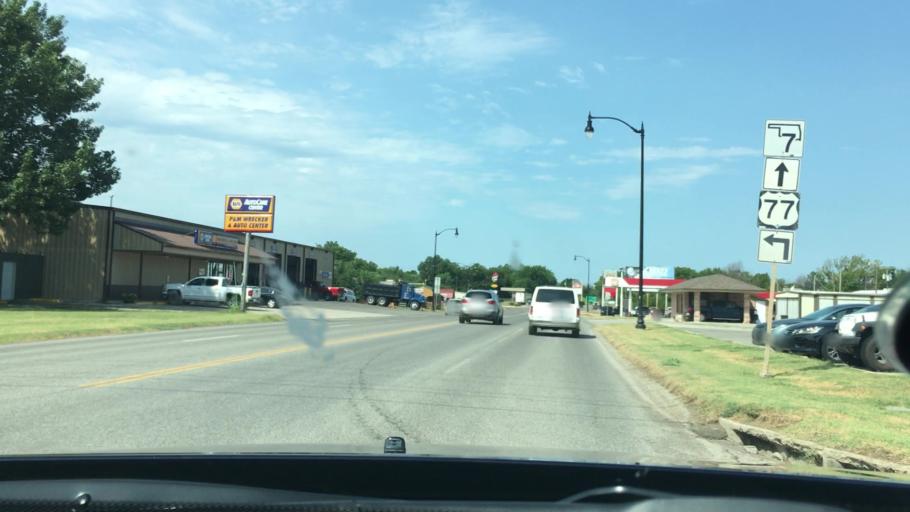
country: US
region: Oklahoma
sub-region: Murray County
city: Davis
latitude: 34.5032
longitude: -97.1240
